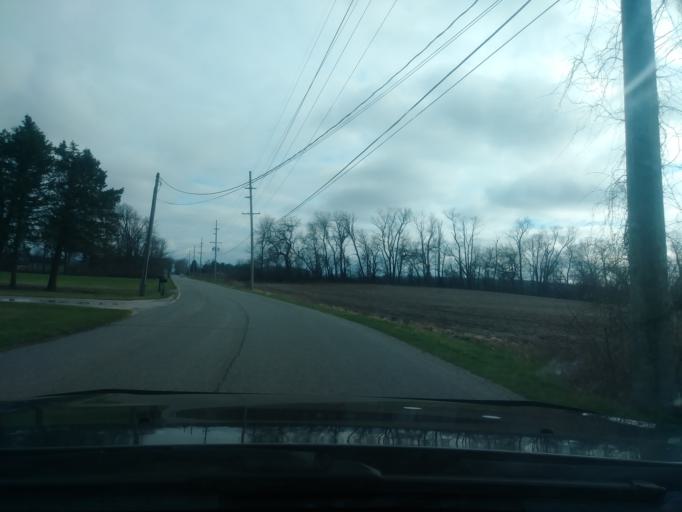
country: US
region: Indiana
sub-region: LaPorte County
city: LaPorte
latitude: 41.6062
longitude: -86.7977
